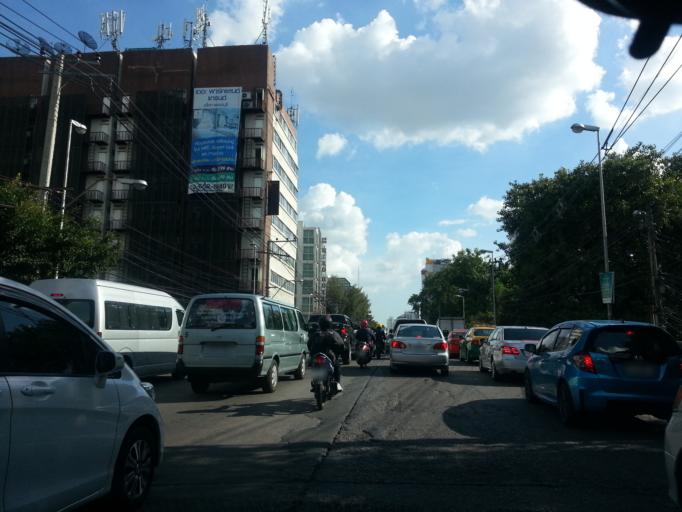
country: TH
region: Bangkok
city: Din Daeng
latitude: 13.7485
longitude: 100.5542
